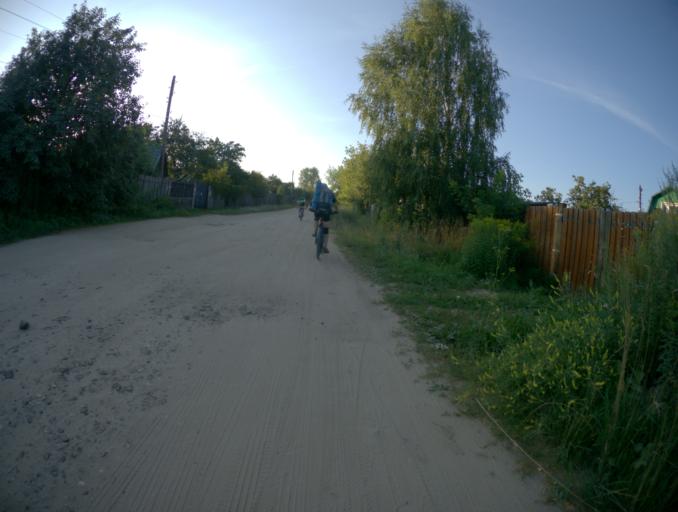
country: RU
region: Nizjnij Novgorod
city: Neklyudovo
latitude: 56.4517
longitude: 44.0073
